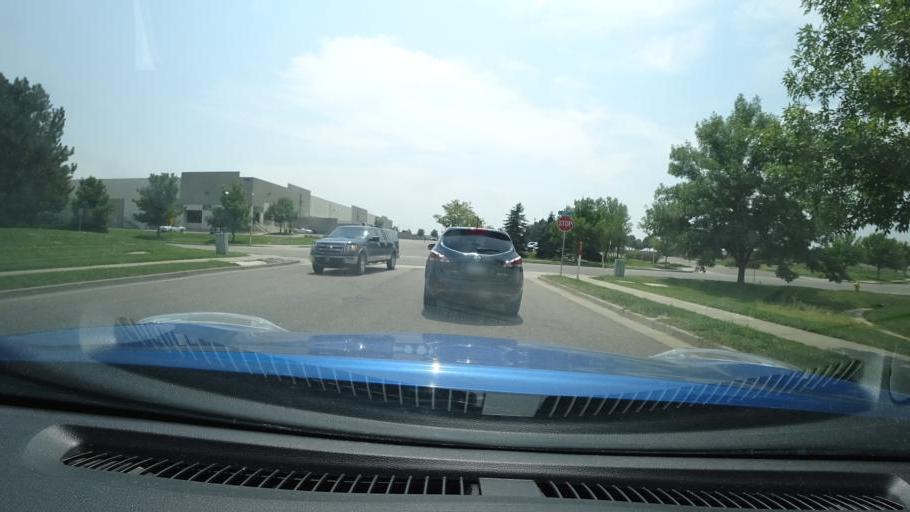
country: US
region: Colorado
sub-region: Adams County
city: Aurora
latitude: 39.7615
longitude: -104.7610
